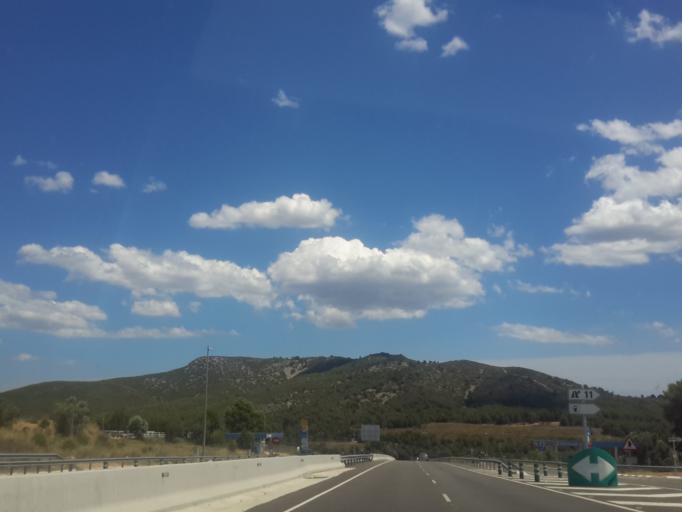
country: ES
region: Catalonia
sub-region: Provincia de Barcelona
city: Vilafranca del Penedes
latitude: 41.3232
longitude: 1.7177
